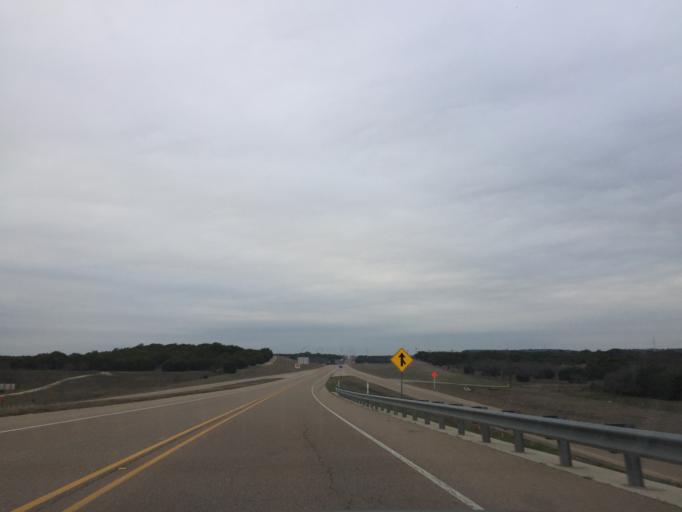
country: US
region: Texas
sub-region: Coryell County
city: Gatesville
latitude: 31.4845
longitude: -97.7355
